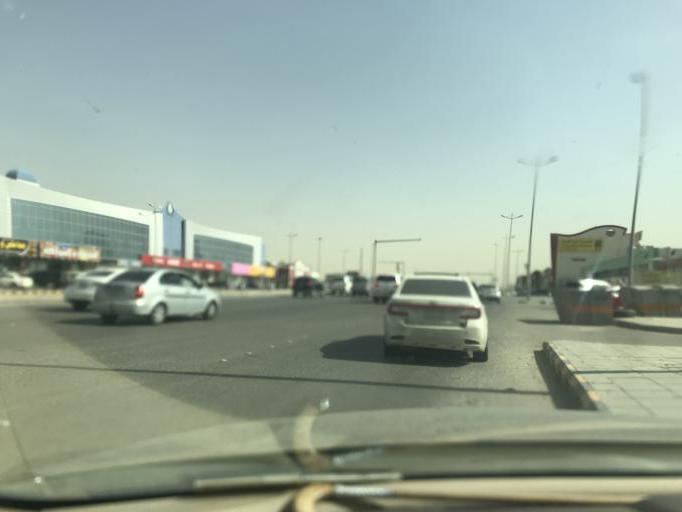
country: SA
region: Ar Riyad
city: Riyadh
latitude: 24.8021
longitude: 46.7391
